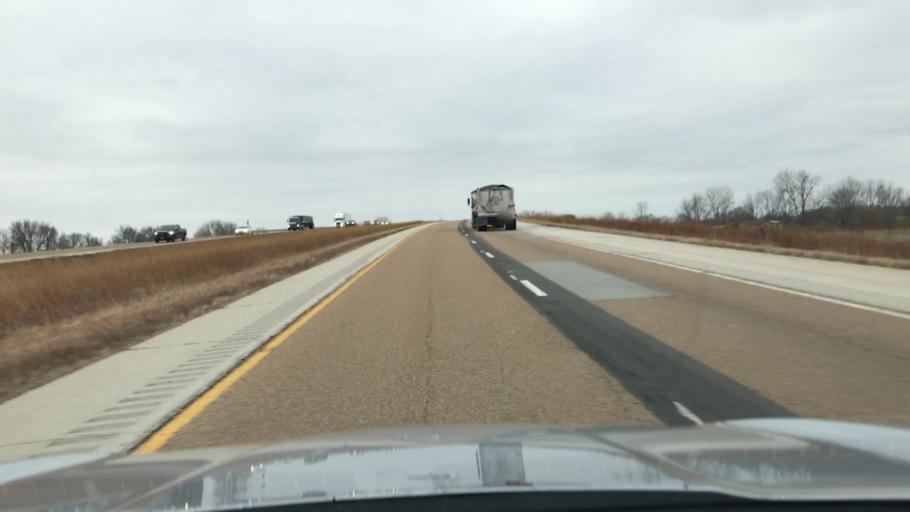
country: US
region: Illinois
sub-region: Montgomery County
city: Litchfield
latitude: 39.2205
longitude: -89.6481
